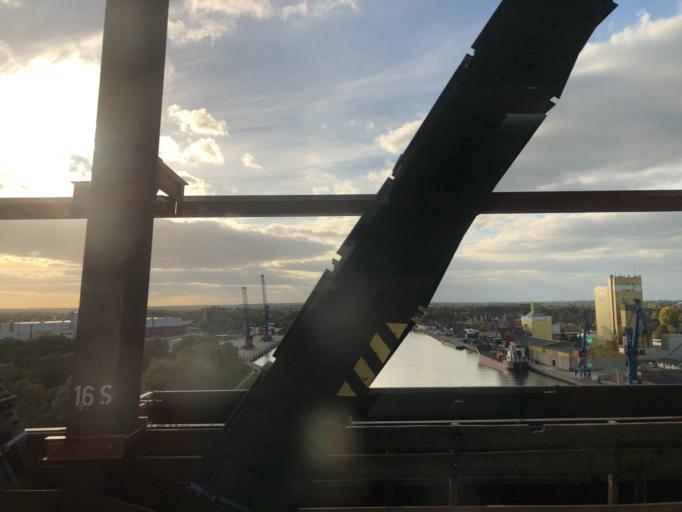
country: DE
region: Schleswig-Holstein
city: Osterronfeld
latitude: 54.2932
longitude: 9.6829
